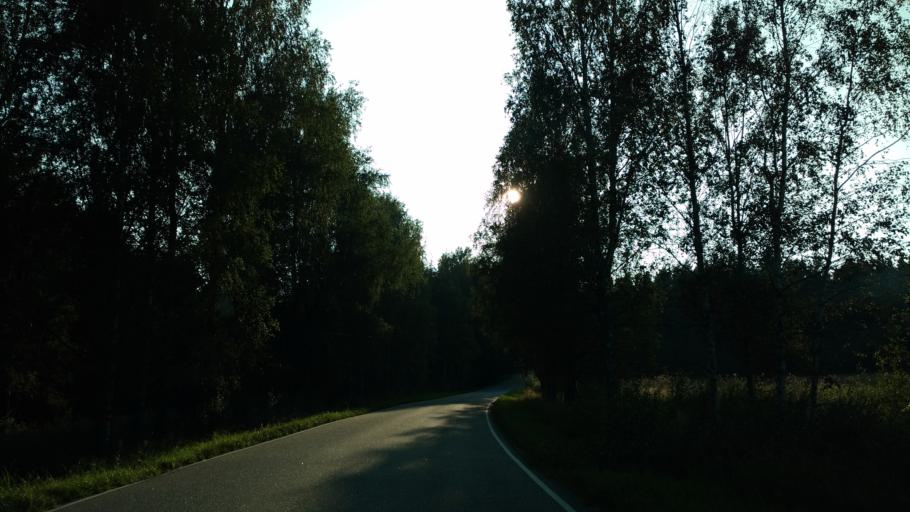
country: FI
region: Varsinais-Suomi
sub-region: Aboland-Turunmaa
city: Dragsfjaerd
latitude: 60.0283
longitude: 22.4572
